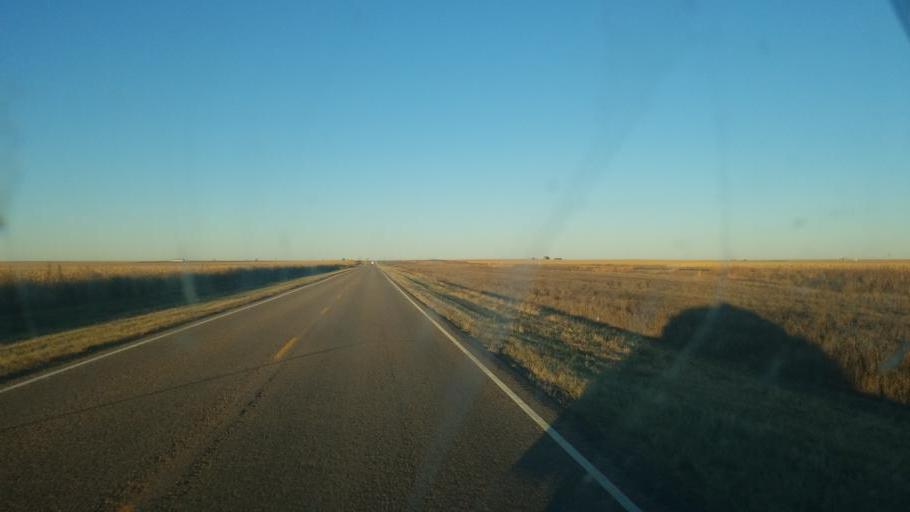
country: US
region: Colorado
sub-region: Cheyenne County
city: Cheyenne Wells
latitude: 38.8506
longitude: -102.0932
